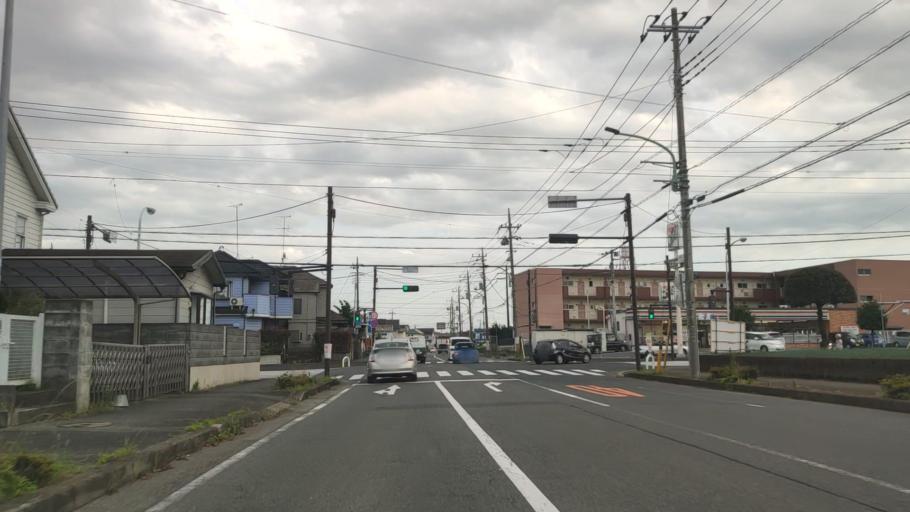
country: JP
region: Tokyo
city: Ome
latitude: 35.7970
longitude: 139.2980
